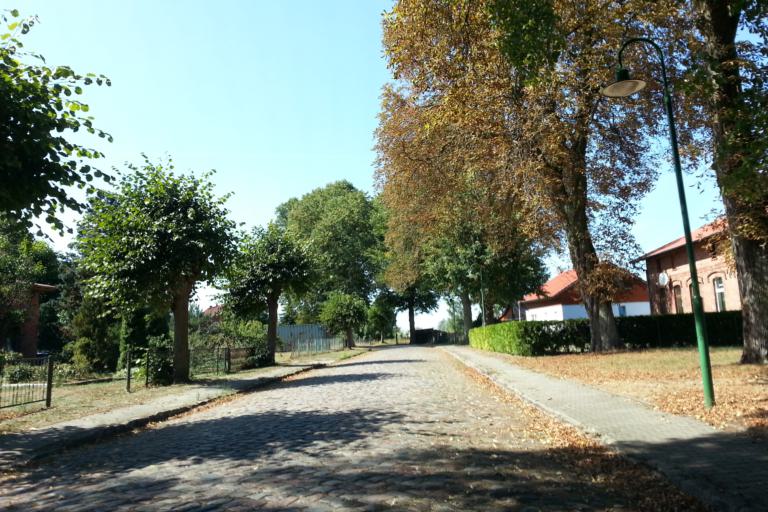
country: DE
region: Mecklenburg-Vorpommern
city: Ferdinandshof
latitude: 53.6452
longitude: 13.9189
